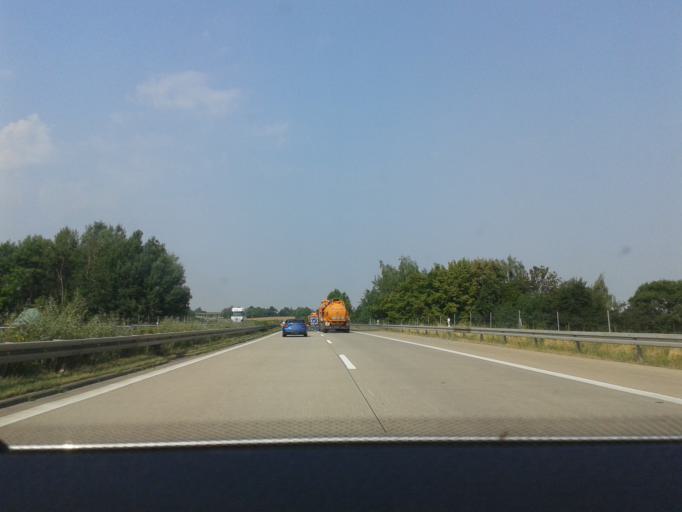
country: DE
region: Saxony
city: Grossweitzschen
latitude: 51.1673
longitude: 13.0836
